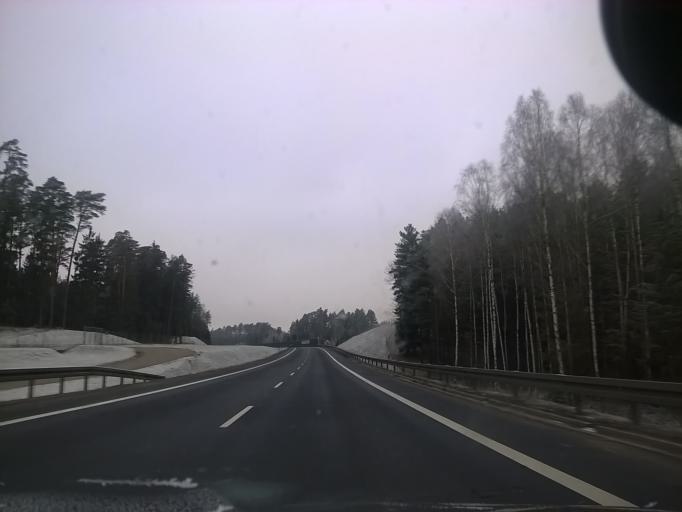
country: PL
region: Warmian-Masurian Voivodeship
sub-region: Powiat olsztynski
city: Barczewo
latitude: 53.8407
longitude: 20.7479
